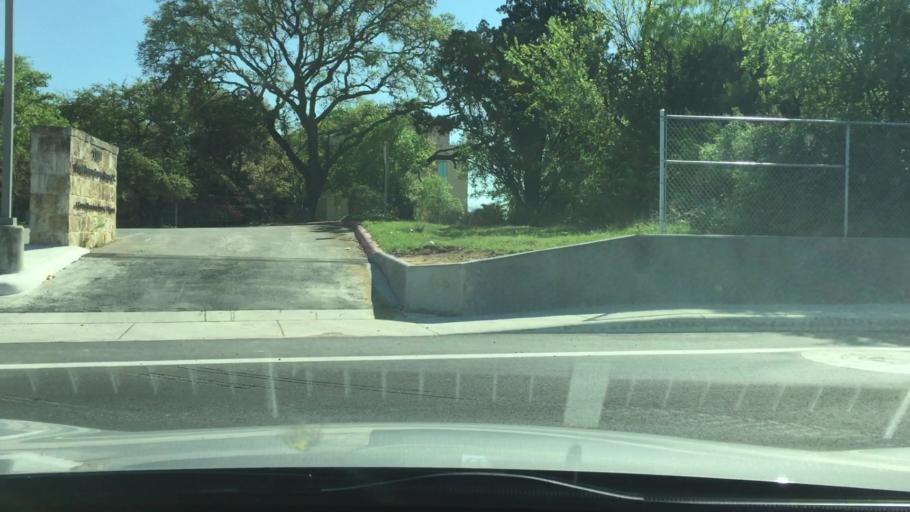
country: US
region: Texas
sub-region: Bexar County
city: Hollywood Park
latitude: 29.5983
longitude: -98.4401
